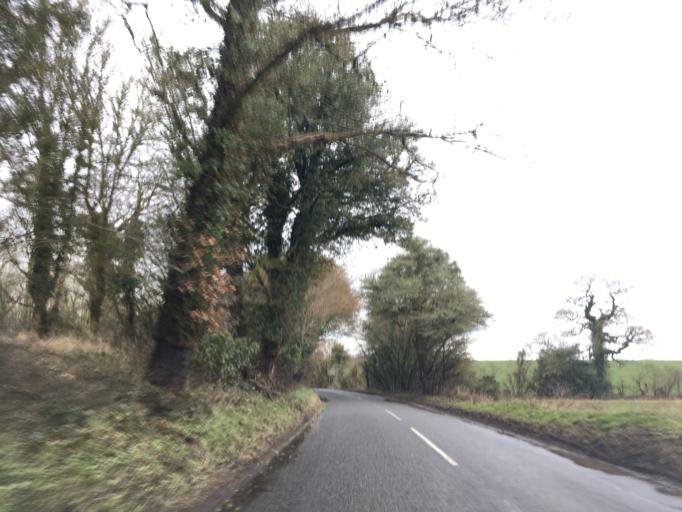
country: GB
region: England
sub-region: Wiltshire
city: Chilton Foliat
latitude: 51.4564
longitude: -1.5286
